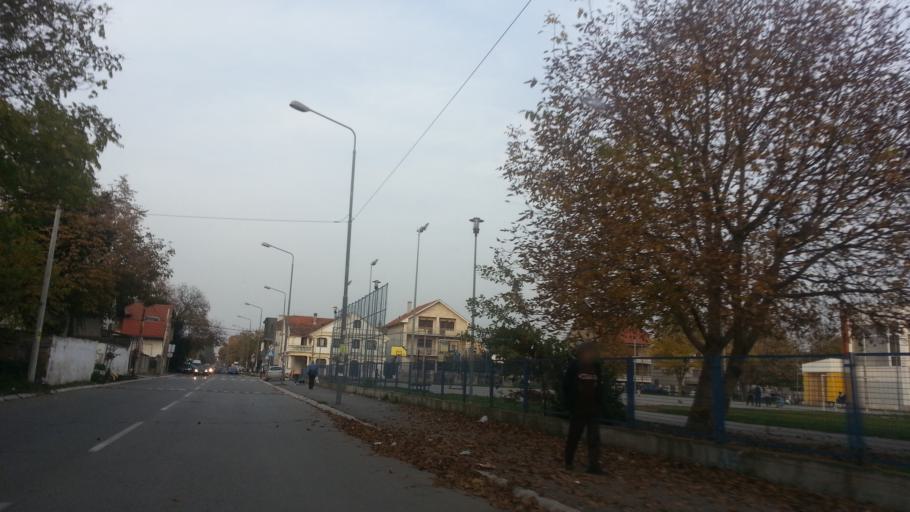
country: RS
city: Novi Banovci
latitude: 44.9007
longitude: 20.2800
